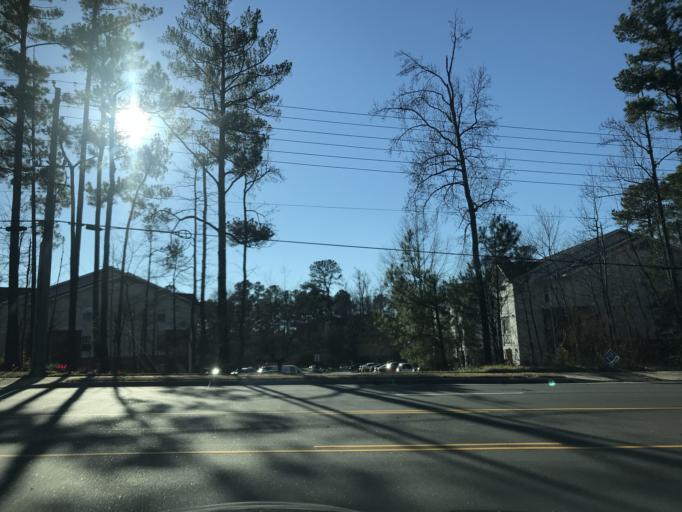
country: US
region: North Carolina
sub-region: Wake County
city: Morrisville
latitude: 35.8992
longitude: -78.8075
